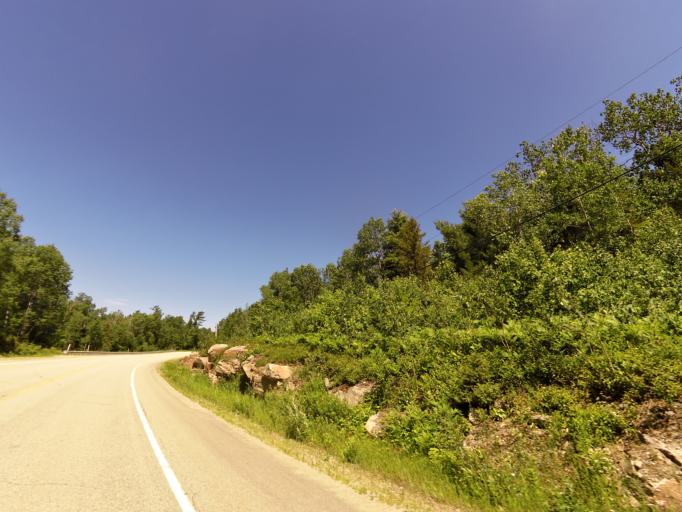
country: CA
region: Quebec
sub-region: Abitibi-Temiscamingue
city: Temiscaming
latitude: 46.7500
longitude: -79.0758
